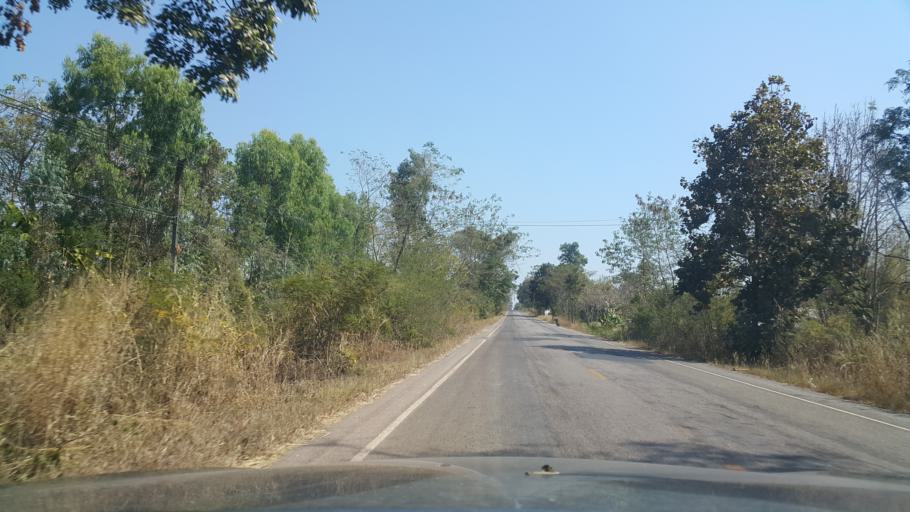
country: TH
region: Changwat Udon Thani
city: Ban Dung
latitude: 17.6091
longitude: 103.2976
